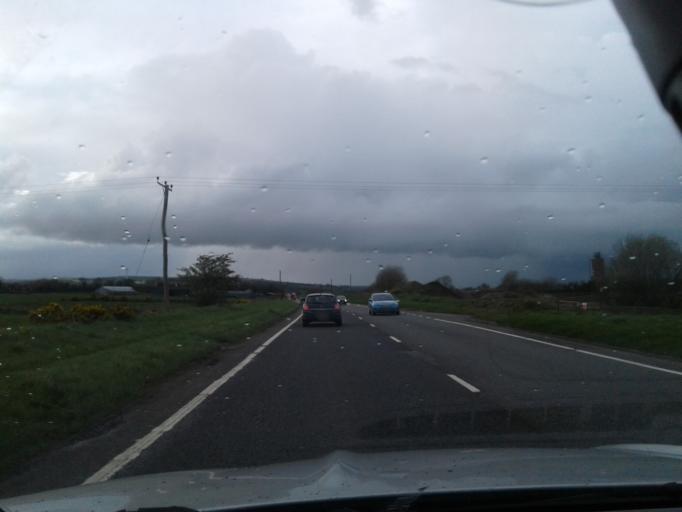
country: GB
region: Northern Ireland
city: Newtownstewart
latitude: 54.7283
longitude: -7.4101
